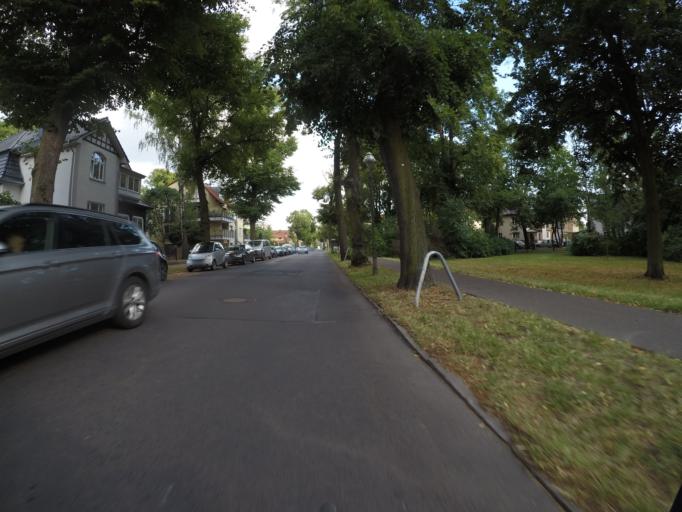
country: DE
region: Berlin
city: Kaulsdorf
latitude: 52.5098
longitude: 13.5891
